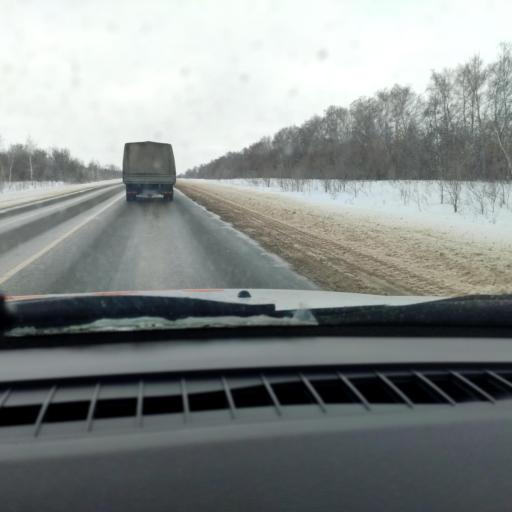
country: RU
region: Samara
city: Dubovyy Umet
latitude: 52.6387
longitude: 50.4896
